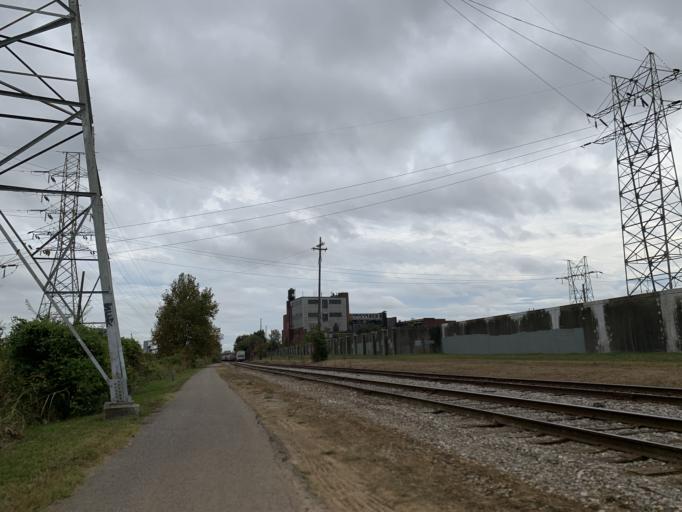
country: US
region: Kentucky
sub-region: Jefferson County
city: Louisville
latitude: 38.2710
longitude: -85.7803
